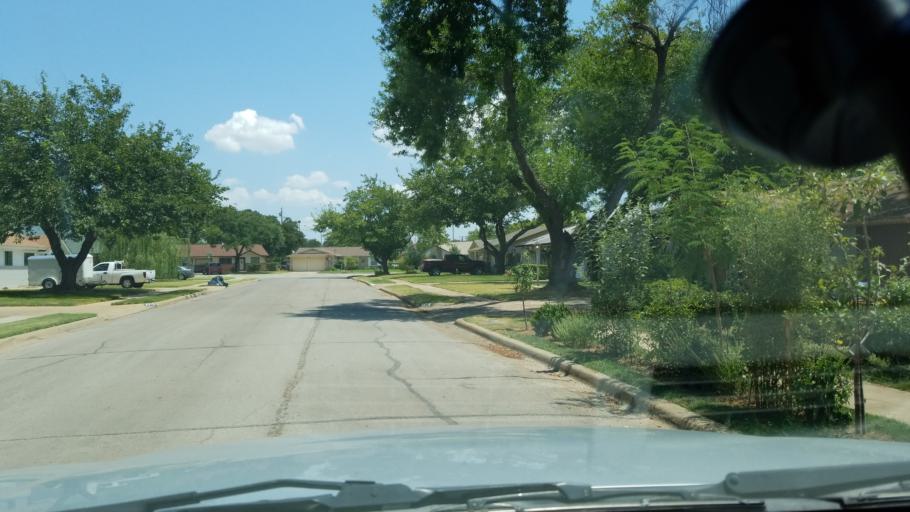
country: US
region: Texas
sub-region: Dallas County
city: Irving
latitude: 32.8223
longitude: -96.9890
